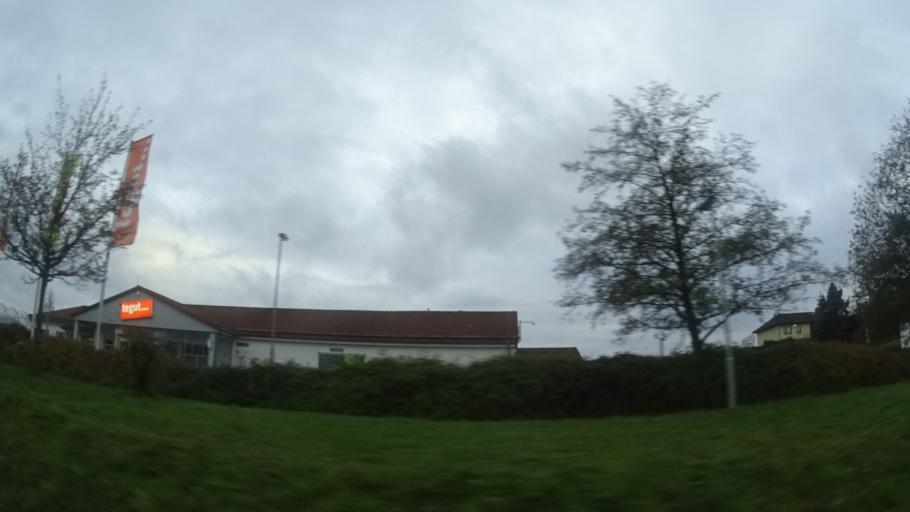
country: DE
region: Hesse
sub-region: Regierungsbezirk Giessen
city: Freiensteinau
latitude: 50.4218
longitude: 9.4121
